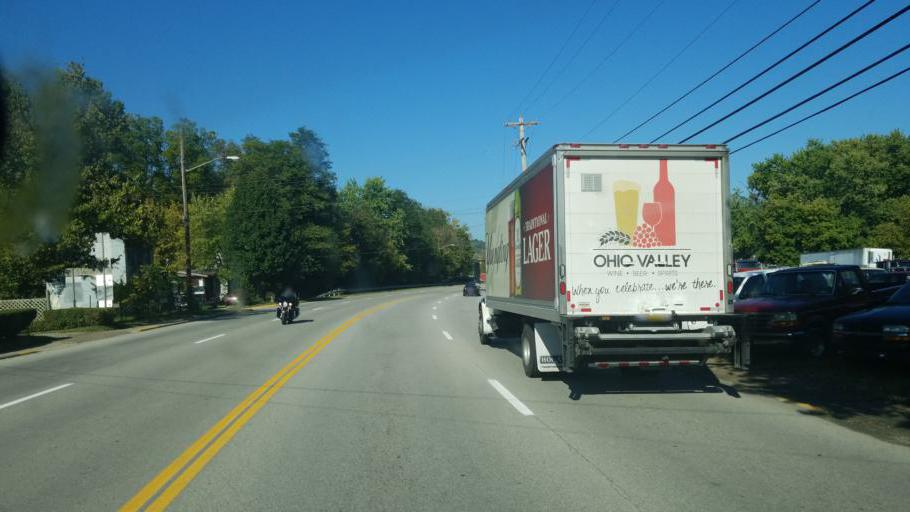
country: US
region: Ohio
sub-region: Brown County
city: Aberdeen
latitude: 38.6562
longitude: -83.7631
